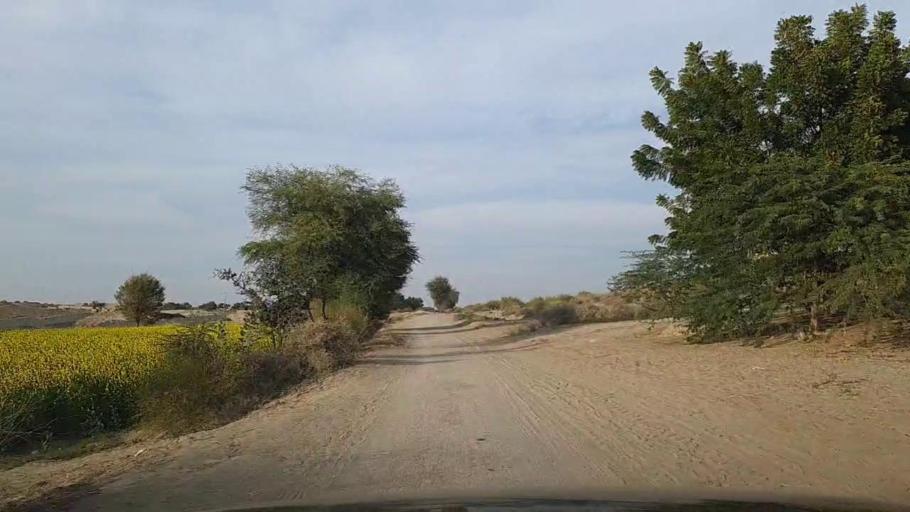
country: PK
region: Sindh
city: Jam Sahib
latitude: 26.4565
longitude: 68.5699
